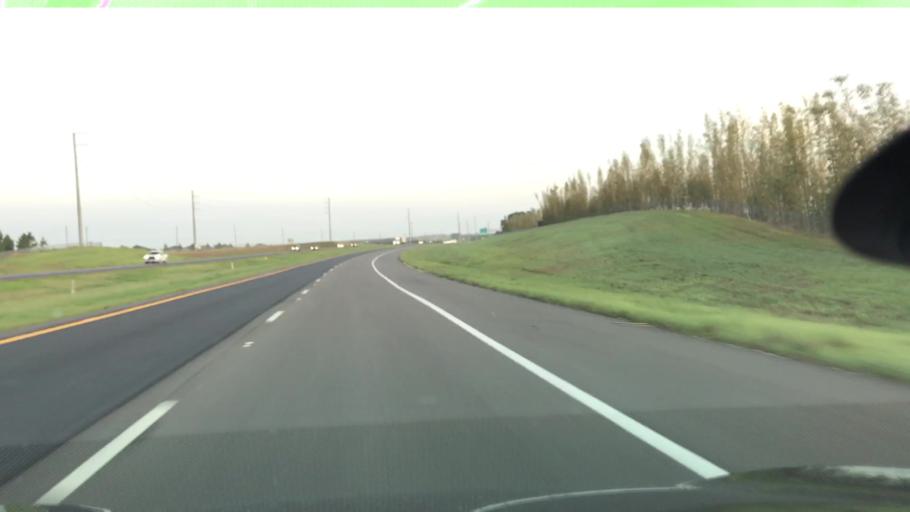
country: US
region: Florida
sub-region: Polk County
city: Citrus Ridge
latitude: 28.4223
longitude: -81.6335
